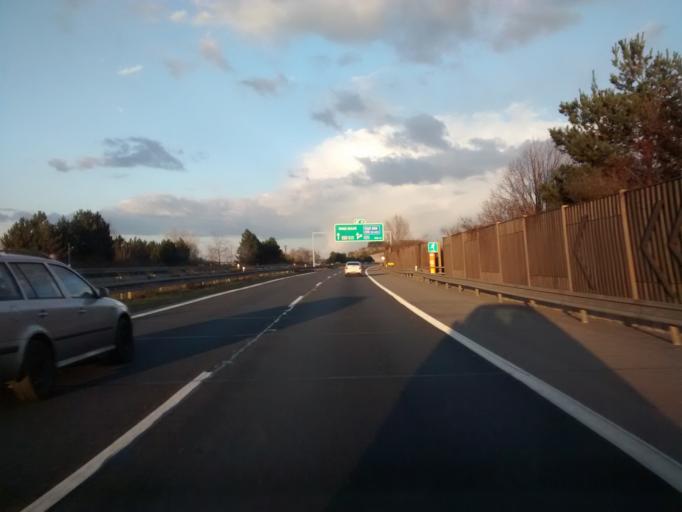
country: CZ
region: Central Bohemia
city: Prerov nad Labem
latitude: 50.1372
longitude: 14.8333
